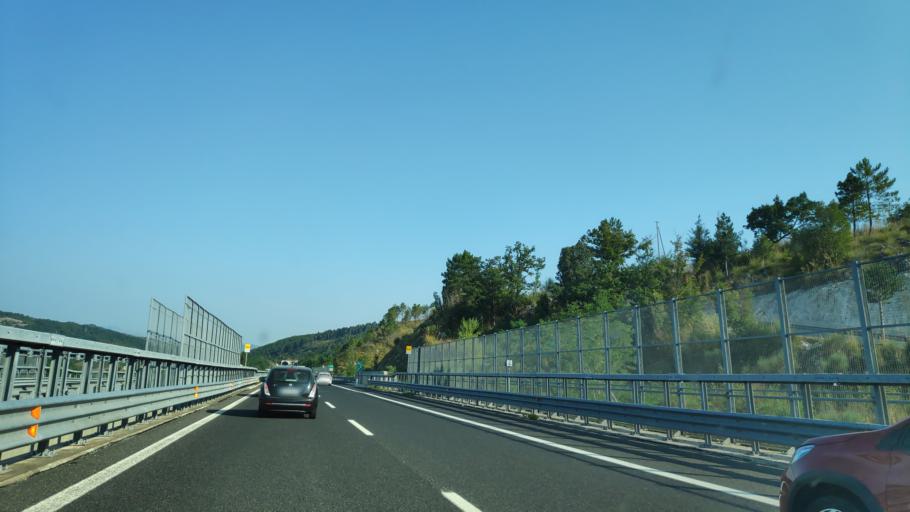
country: IT
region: Campania
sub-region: Provincia di Salerno
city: Casalbuono
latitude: 40.1767
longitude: 15.7167
